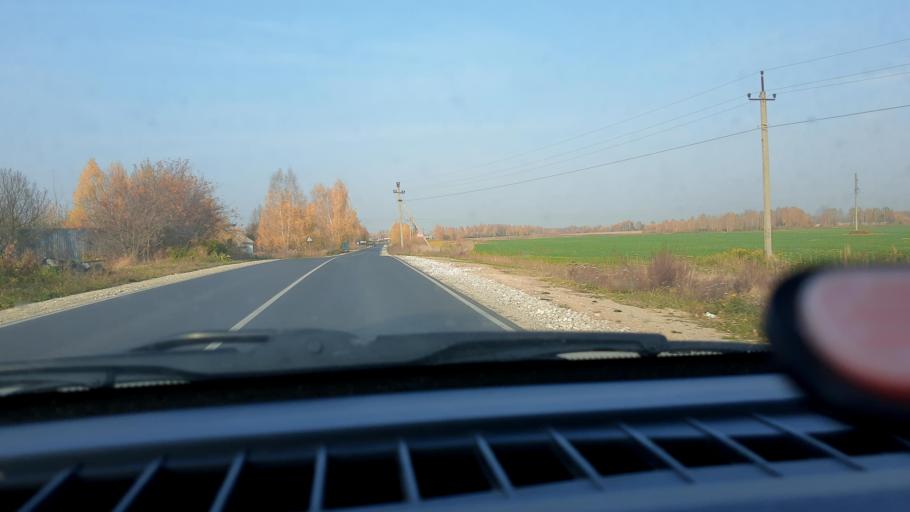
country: RU
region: Nizjnij Novgorod
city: Neklyudovo
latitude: 56.4456
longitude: 43.8990
